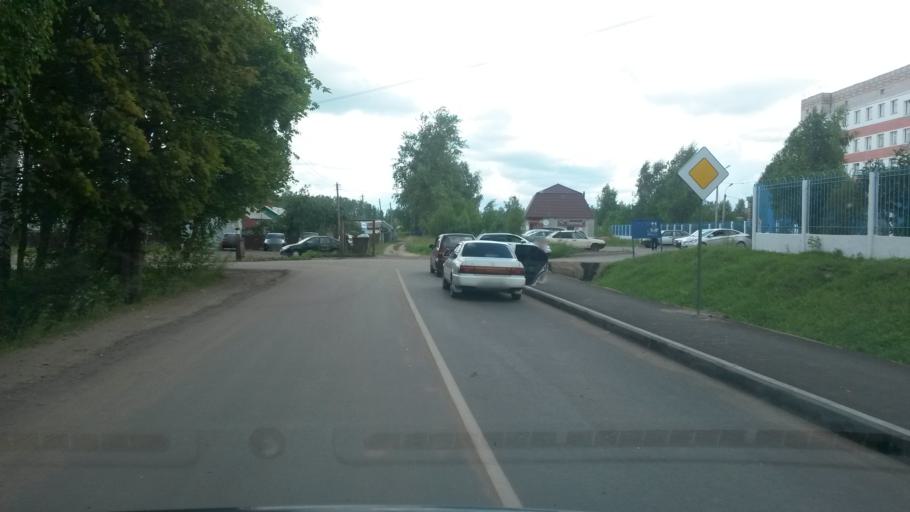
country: RU
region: Jaroslavl
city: Gavrilov-Yam
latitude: 57.3116
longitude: 39.8654
